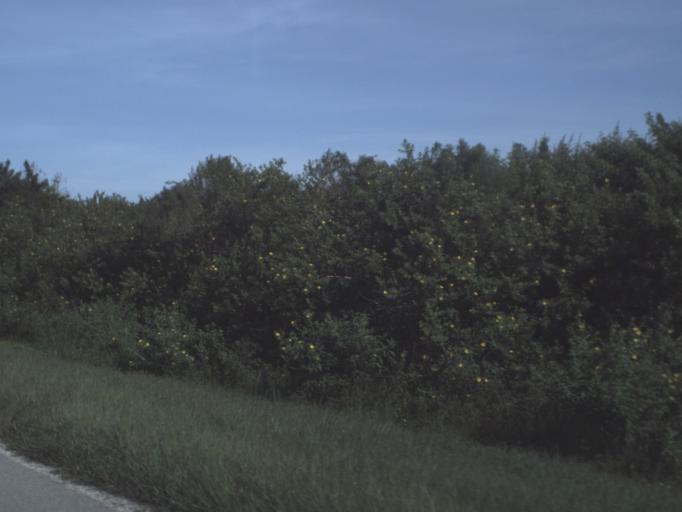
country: US
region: Florida
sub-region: DeSoto County
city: Southeast Arcadia
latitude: 27.1521
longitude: -81.8087
